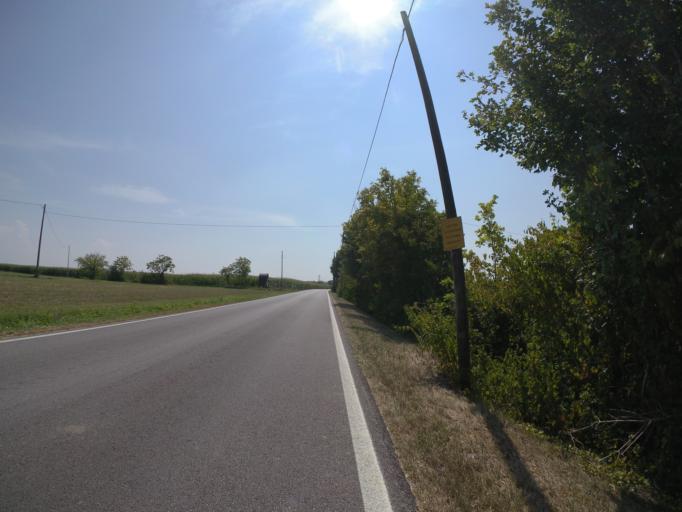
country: IT
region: Friuli Venezia Giulia
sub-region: Provincia di Udine
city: Pocenia
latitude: 45.8592
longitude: 13.0891
